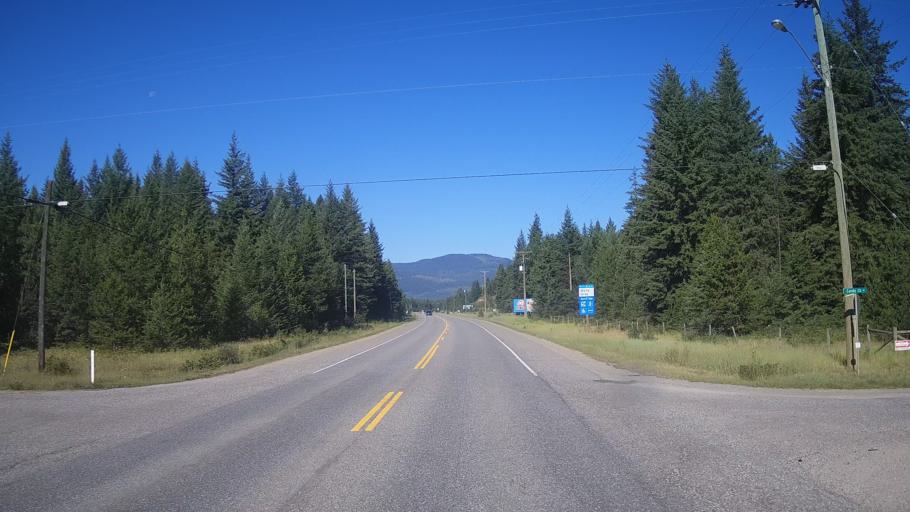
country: CA
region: British Columbia
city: Chase
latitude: 51.6519
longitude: -120.0095
